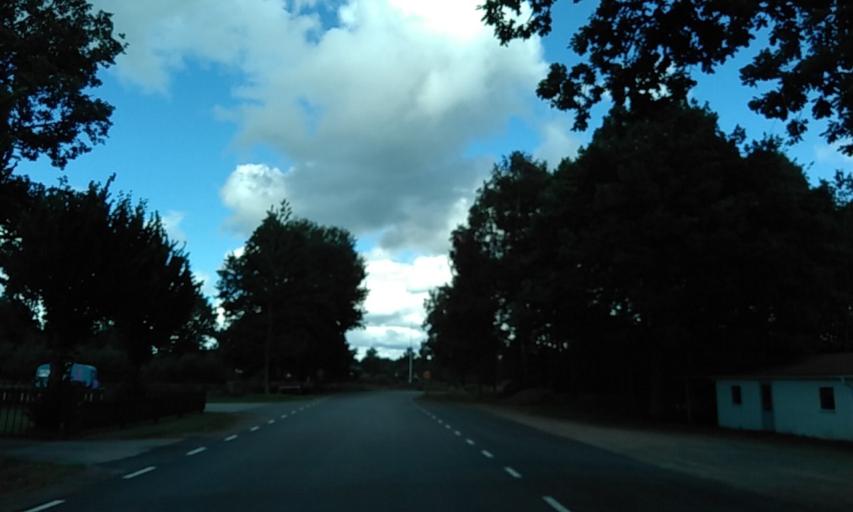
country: SE
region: Vaestra Goetaland
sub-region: Vargarda Kommun
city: Vargarda
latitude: 57.9860
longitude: 12.9264
